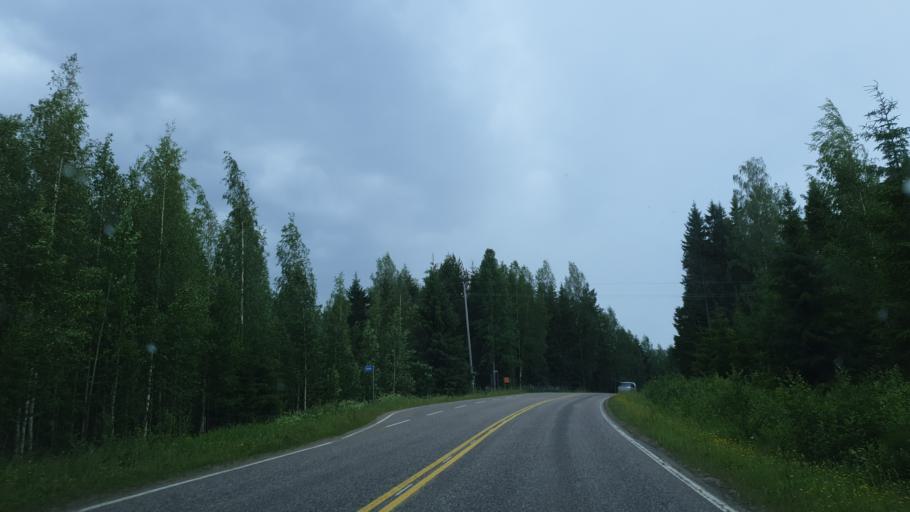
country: FI
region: Northern Savo
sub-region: Kuopio
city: Vehmersalmi
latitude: 62.9268
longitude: 27.9171
